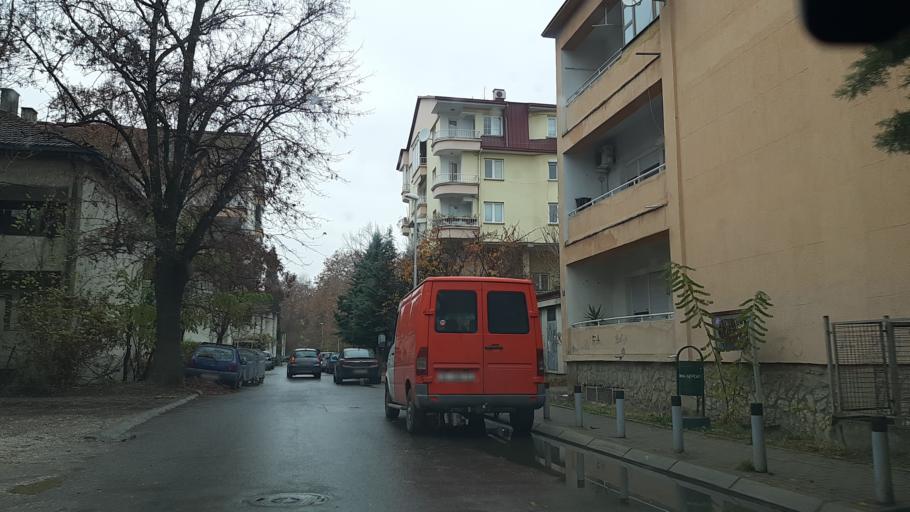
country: MK
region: Karpos
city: Skopje
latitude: 41.9862
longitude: 21.4475
